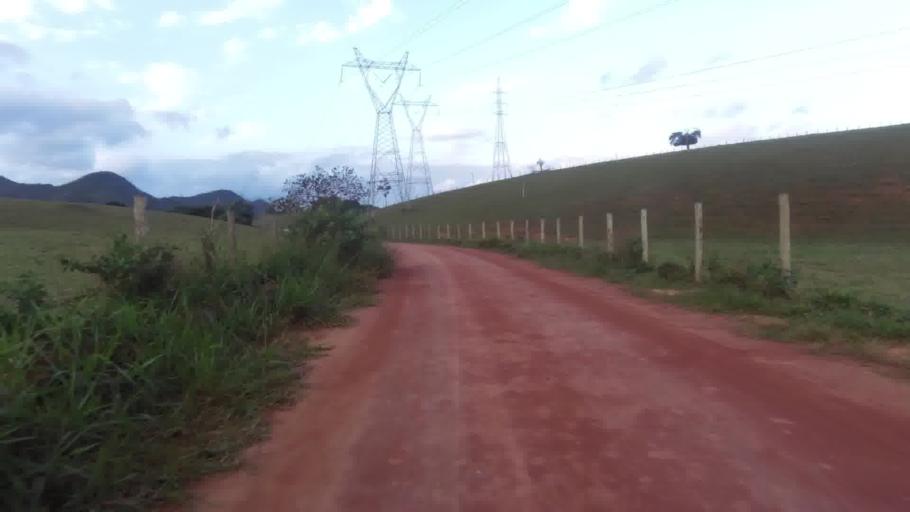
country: BR
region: Espirito Santo
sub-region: Guarapari
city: Guarapari
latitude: -20.6754
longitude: -40.6165
